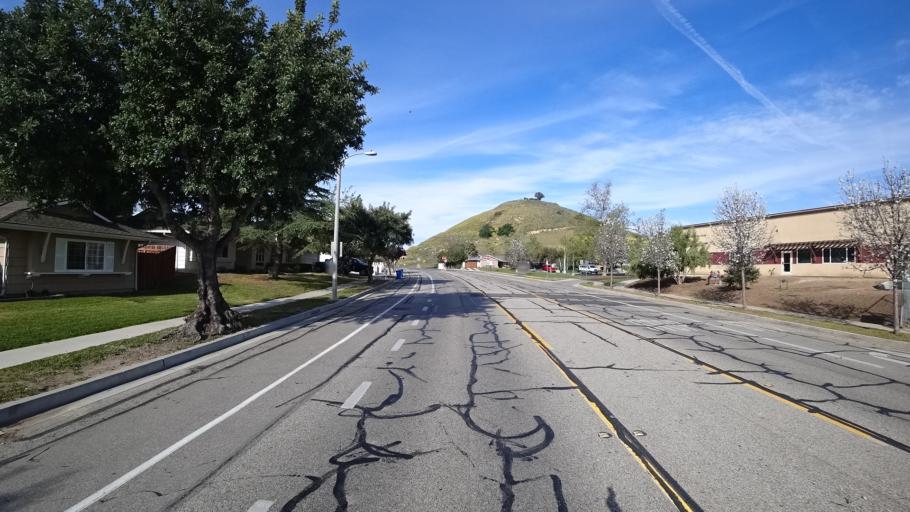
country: US
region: California
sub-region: Ventura County
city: Thousand Oaks
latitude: 34.1966
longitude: -118.8831
